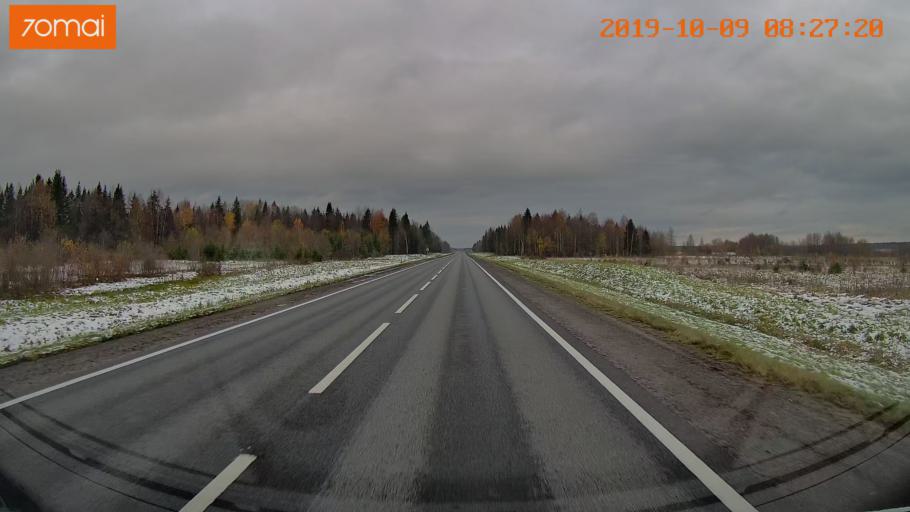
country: RU
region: Vologda
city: Gryazovets
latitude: 58.8024
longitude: 40.2503
